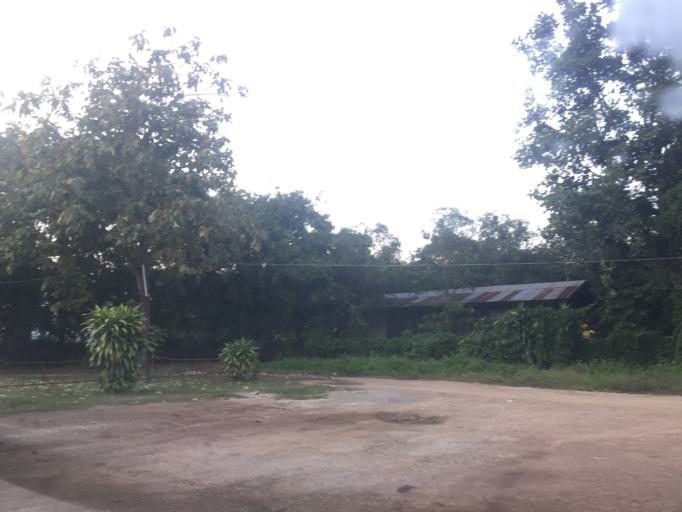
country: TH
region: Chiang Mai
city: Chiang Mai
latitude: 18.8020
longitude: 98.9719
